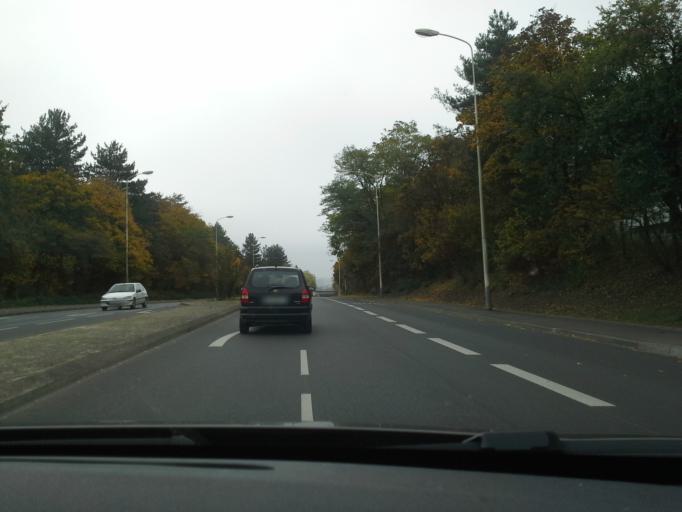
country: FR
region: Centre
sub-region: Departement d'Indre-et-Loire
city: Tours
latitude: 47.4087
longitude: 0.7033
